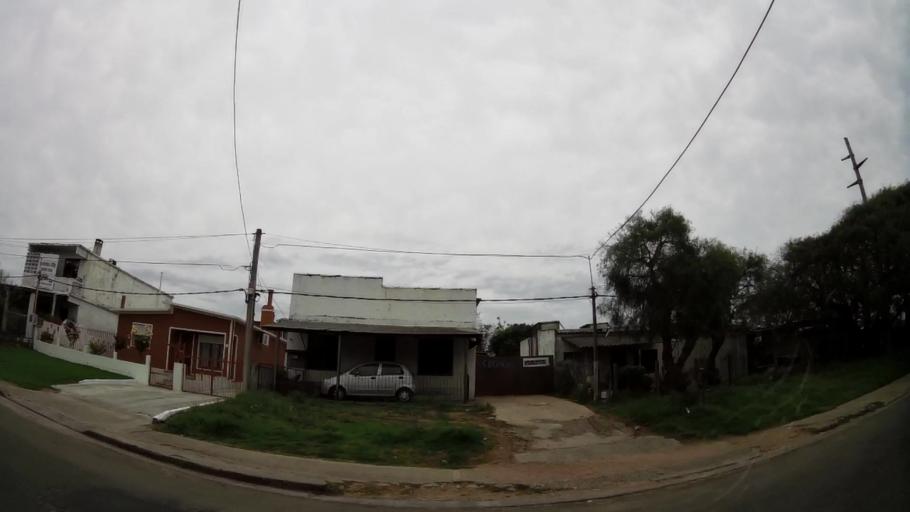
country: UY
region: Maldonado
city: Maldonado
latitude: -34.8939
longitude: -54.9525
